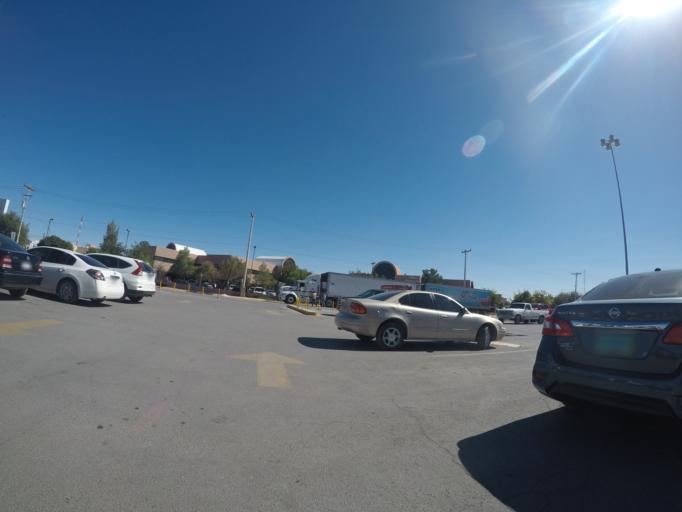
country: MX
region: Chihuahua
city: Ciudad Juarez
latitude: 31.7141
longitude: -106.4205
